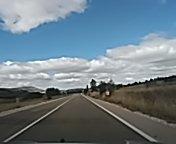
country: ES
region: Castille and Leon
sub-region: Provincia de Burgos
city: Hontoria del Pinar
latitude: 41.8458
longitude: -3.1428
